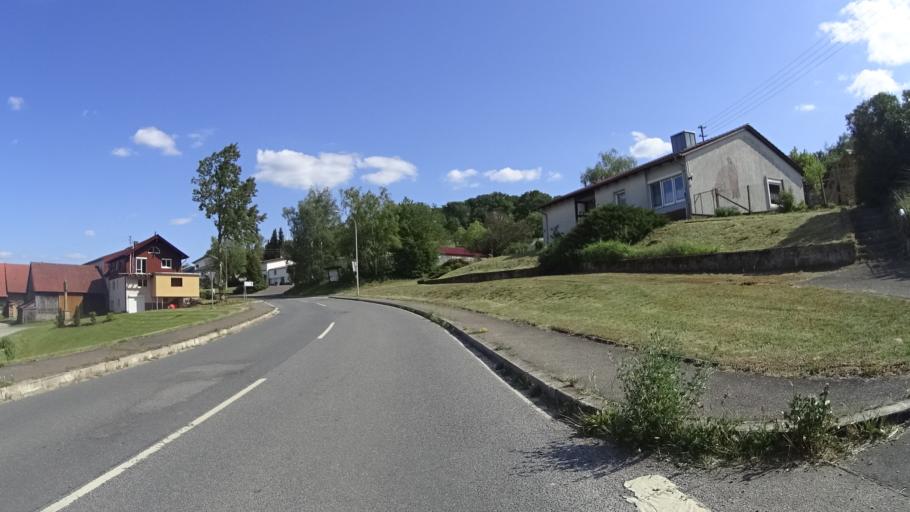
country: DE
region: Baden-Wuerttemberg
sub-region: Regierungsbezirk Stuttgart
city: Buch am Ahorn
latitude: 49.5322
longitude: 9.5084
